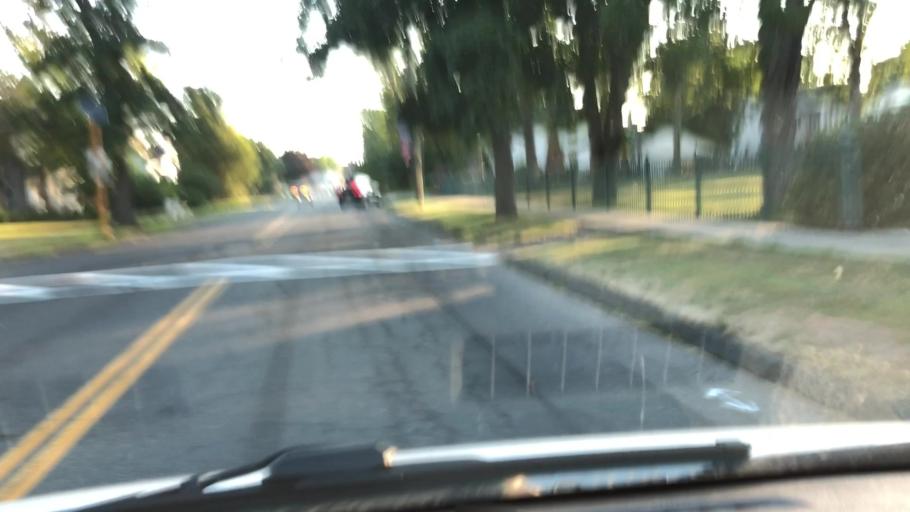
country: US
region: Massachusetts
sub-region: Hampshire County
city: Easthampton
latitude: 42.2666
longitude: -72.6750
